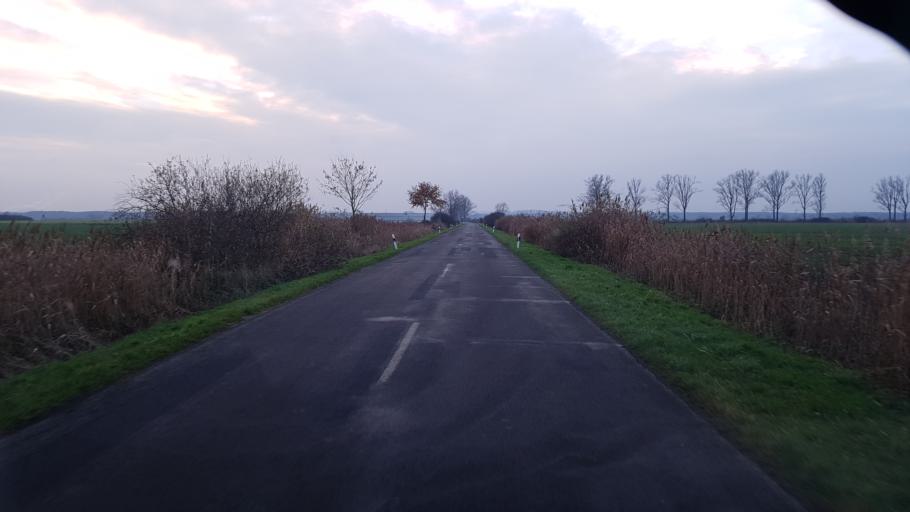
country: DE
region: Brandenburg
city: Ziltendorf
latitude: 52.2216
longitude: 14.6602
